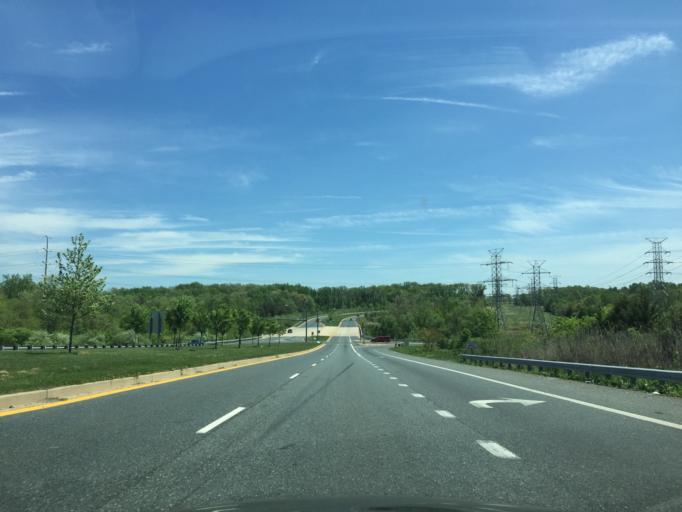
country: US
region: Maryland
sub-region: Baltimore County
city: White Marsh
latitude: 39.3738
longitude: -76.4322
